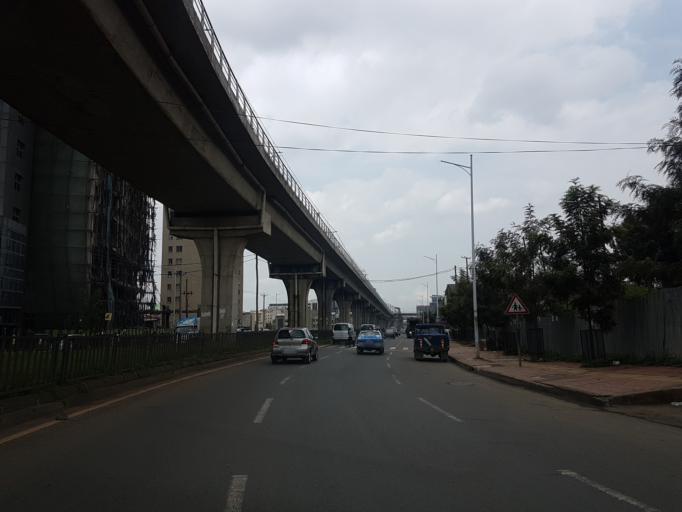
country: ET
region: Adis Abeba
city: Addis Ababa
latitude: 9.0183
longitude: 38.7349
